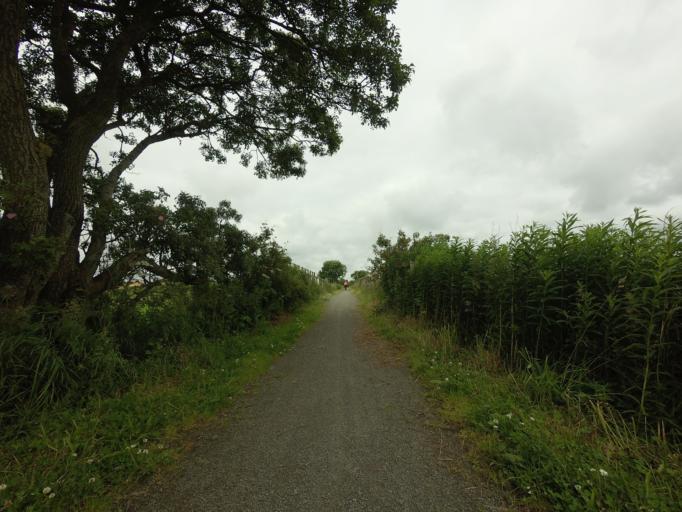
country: GB
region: Scotland
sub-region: Aberdeenshire
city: Ellon
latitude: 57.4694
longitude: -2.1202
